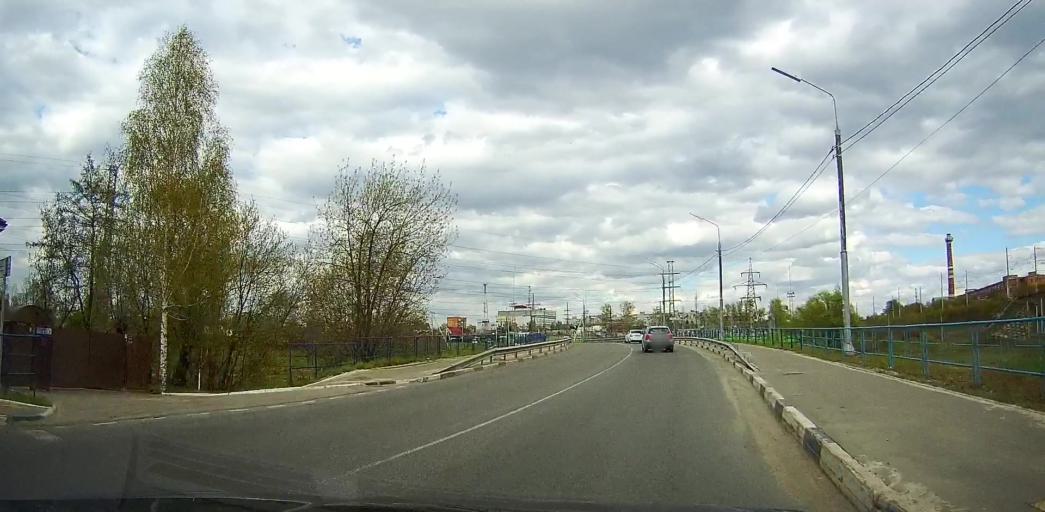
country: RU
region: Moskovskaya
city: Pavlovskiy Posad
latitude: 55.7730
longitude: 38.6434
